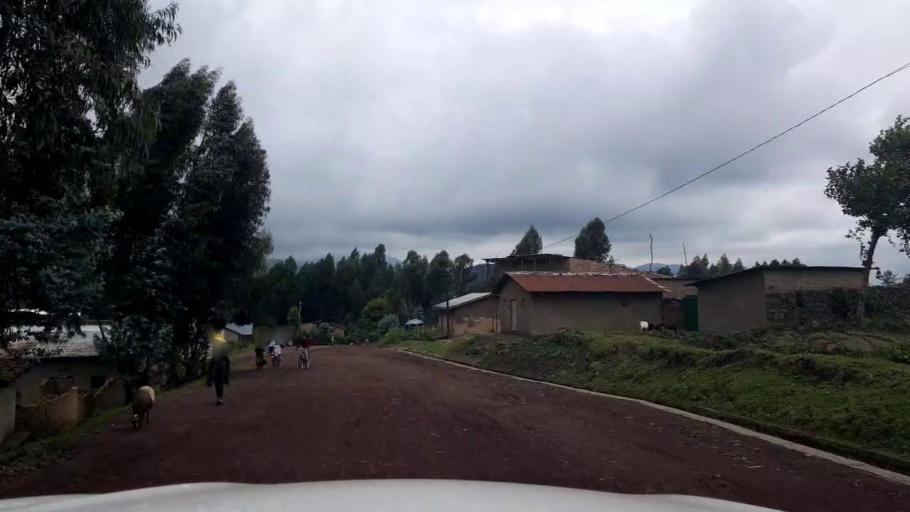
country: RW
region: Northern Province
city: Musanze
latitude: -1.6010
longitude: 29.4521
